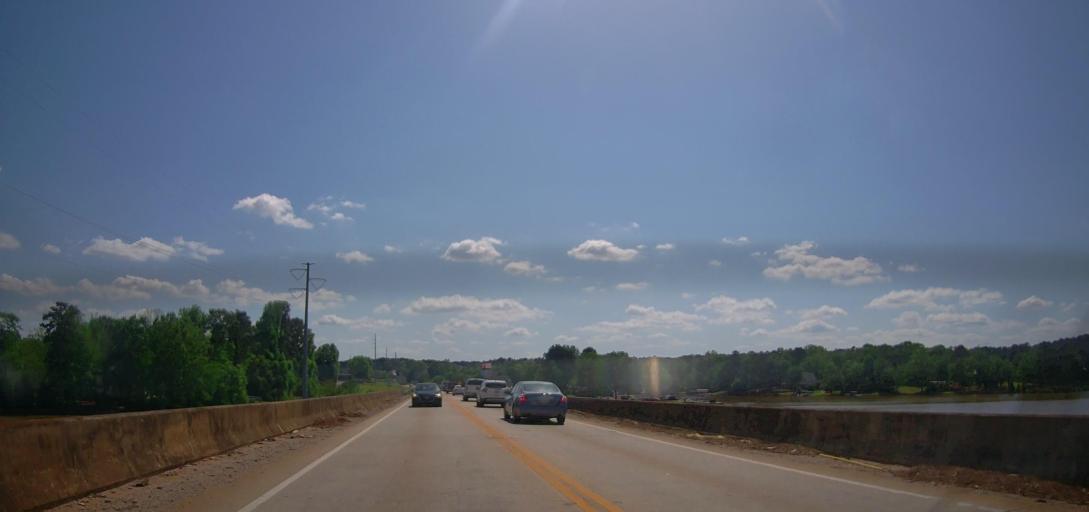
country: US
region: Georgia
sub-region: Putnam County
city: Jefferson
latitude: 33.4435
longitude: -83.2614
